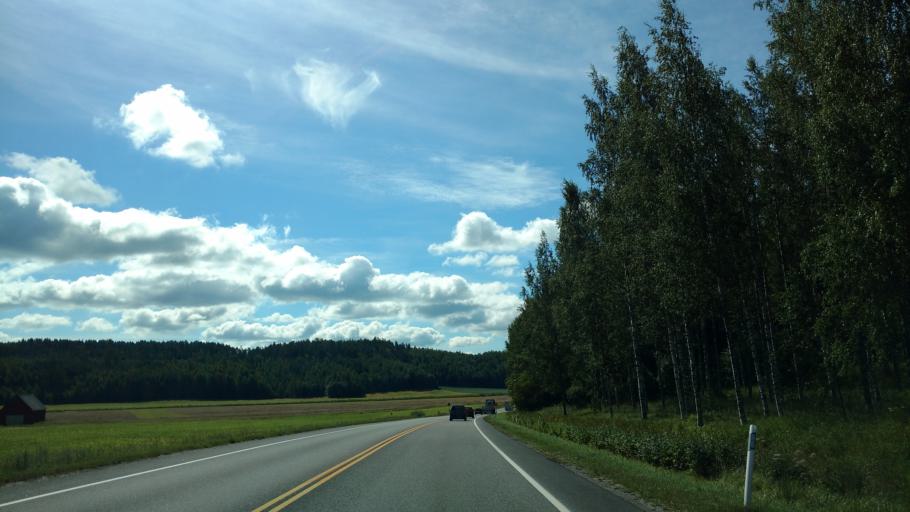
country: FI
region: Varsinais-Suomi
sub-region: Salo
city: Salo
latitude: 60.3628
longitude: 23.1418
